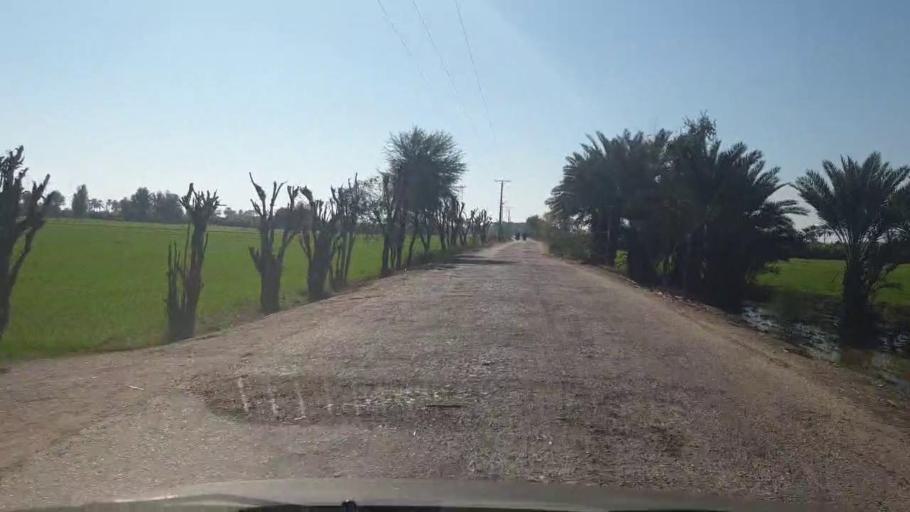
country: PK
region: Sindh
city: Bozdar
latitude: 27.2553
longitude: 68.6524
